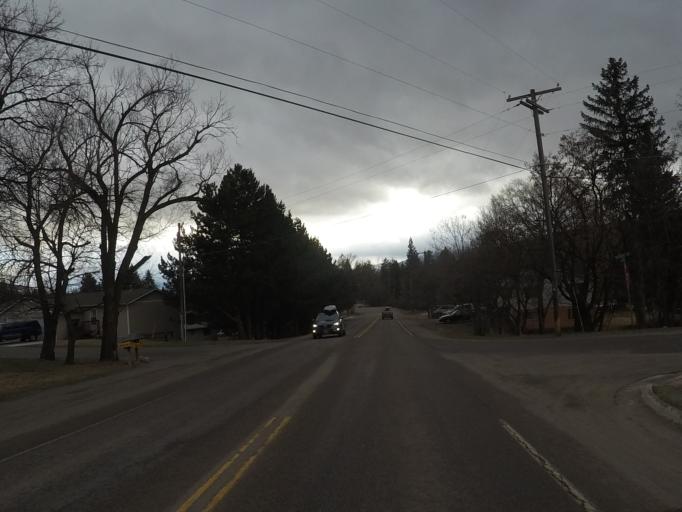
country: US
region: Montana
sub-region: Missoula County
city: East Missoula
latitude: 46.8837
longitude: -113.9672
